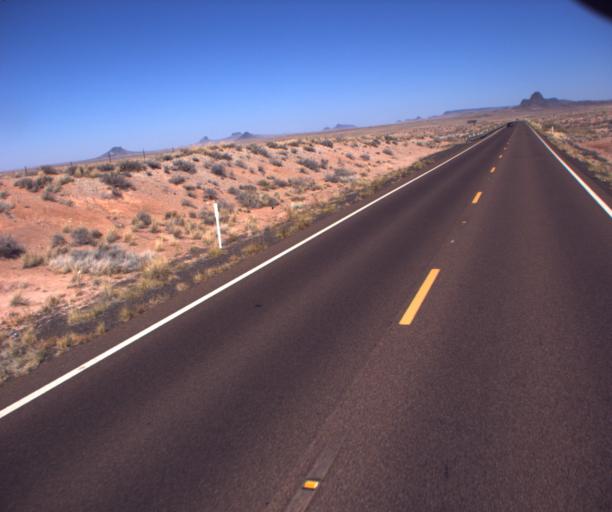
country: US
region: Arizona
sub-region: Navajo County
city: Dilkon
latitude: 35.2213
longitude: -110.4354
